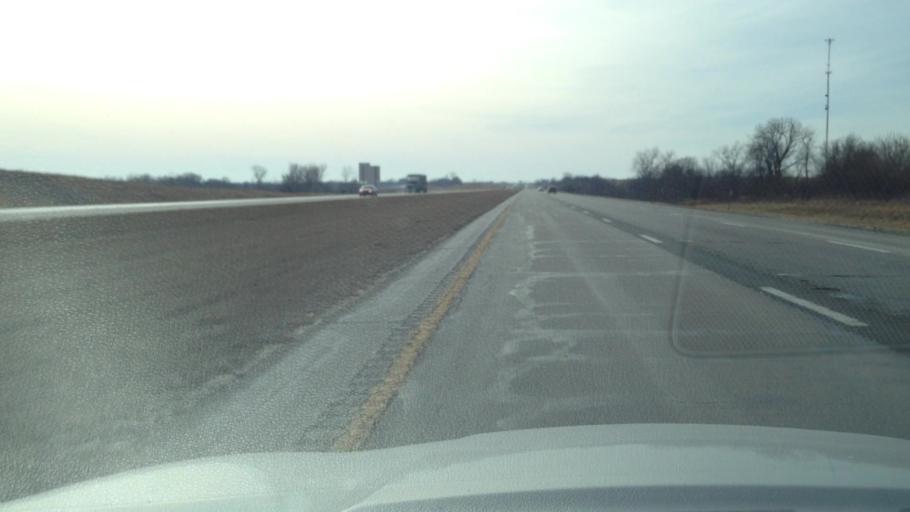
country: US
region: Missouri
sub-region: Harrison County
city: Bethany
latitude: 40.3712
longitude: -94.0040
